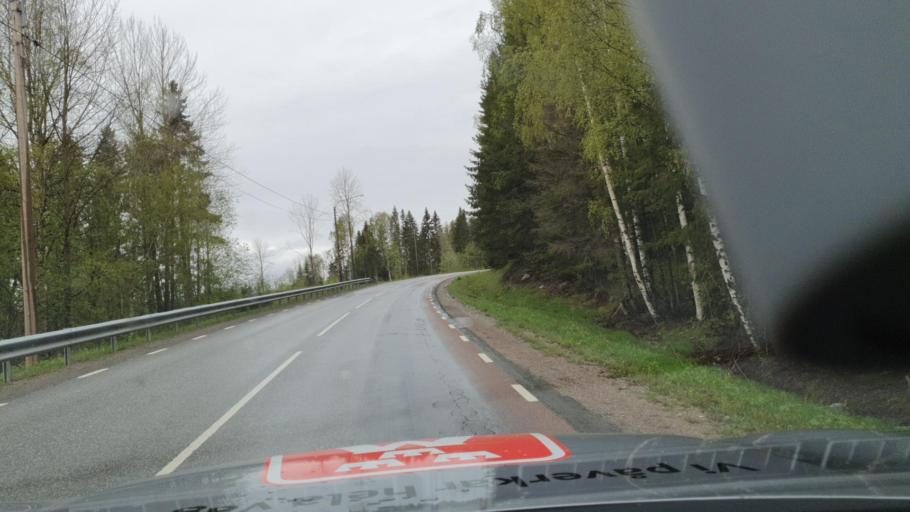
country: SE
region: Vaesternorrland
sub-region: OErnskoeldsviks Kommun
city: Bjasta
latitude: 63.3739
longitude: 18.4801
